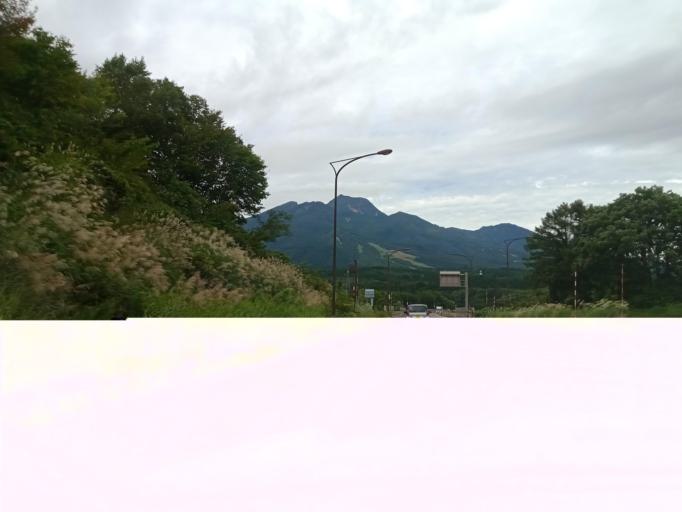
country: JP
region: Niigata
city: Arai
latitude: 36.8491
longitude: 138.1962
